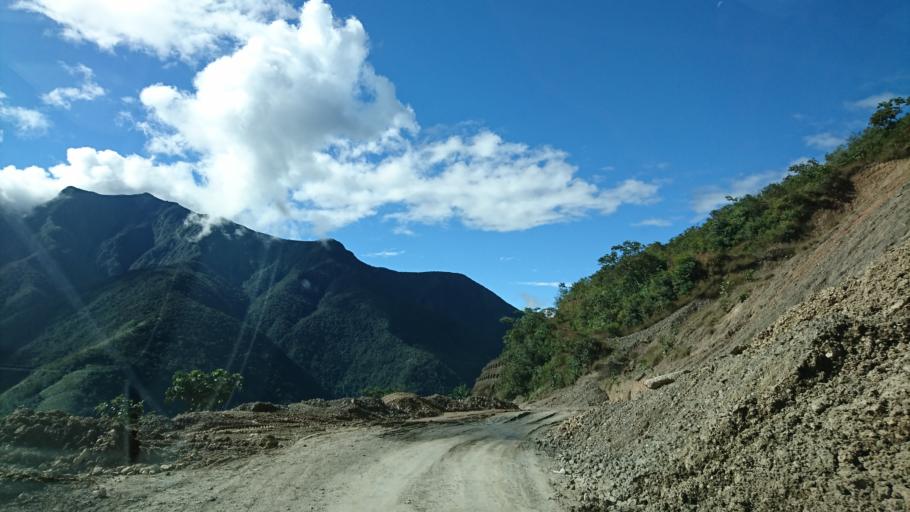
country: BO
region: La Paz
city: Coroico
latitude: -16.2102
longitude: -67.7894
